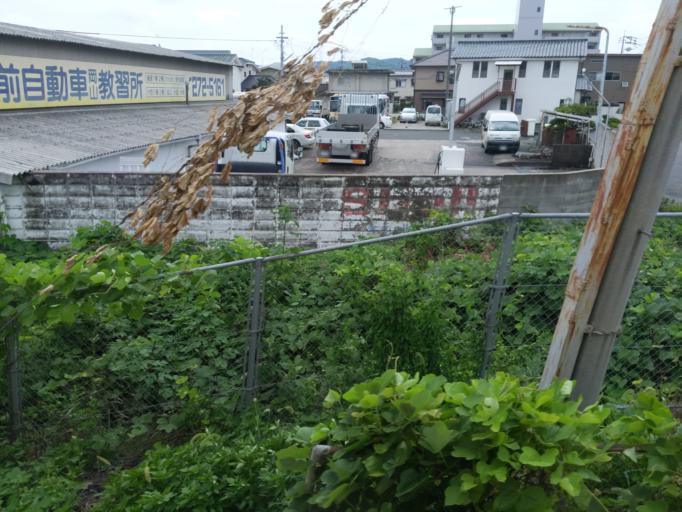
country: JP
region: Okayama
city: Okayama-shi
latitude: 34.6832
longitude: 133.9597
